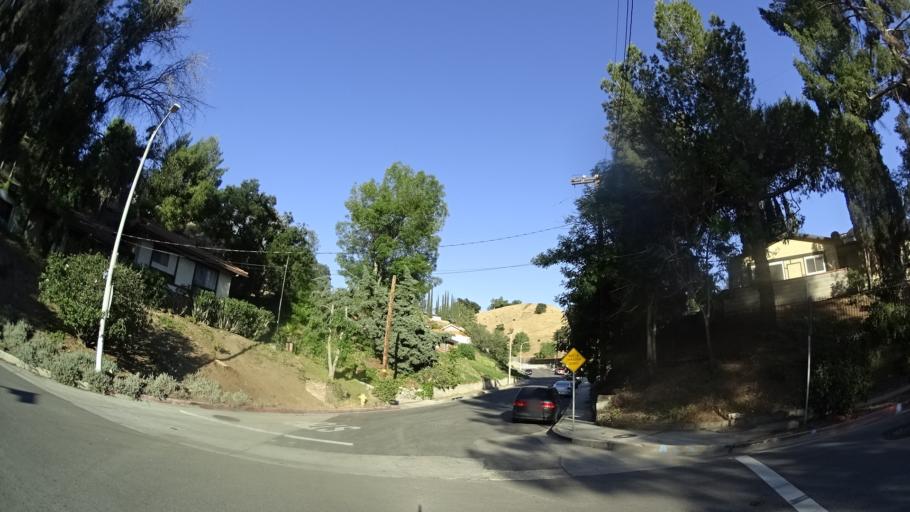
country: US
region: California
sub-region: Los Angeles County
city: La Crescenta-Montrose
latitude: 34.2729
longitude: -118.3023
